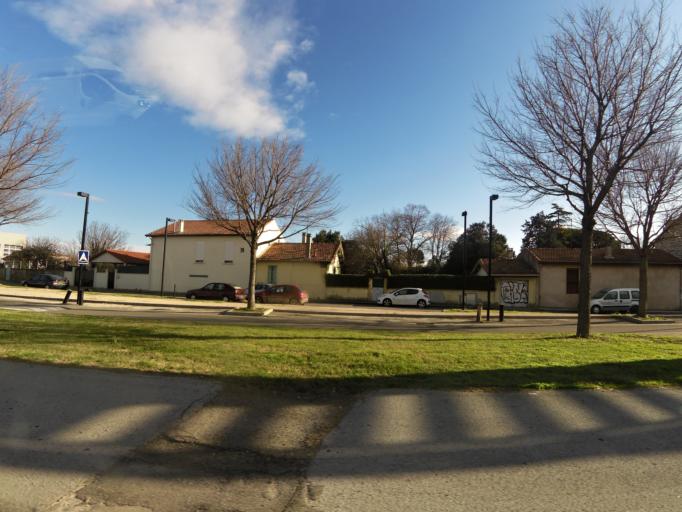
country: FR
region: Languedoc-Roussillon
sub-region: Departement du Gard
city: Nimes
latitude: 43.8289
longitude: 4.3775
